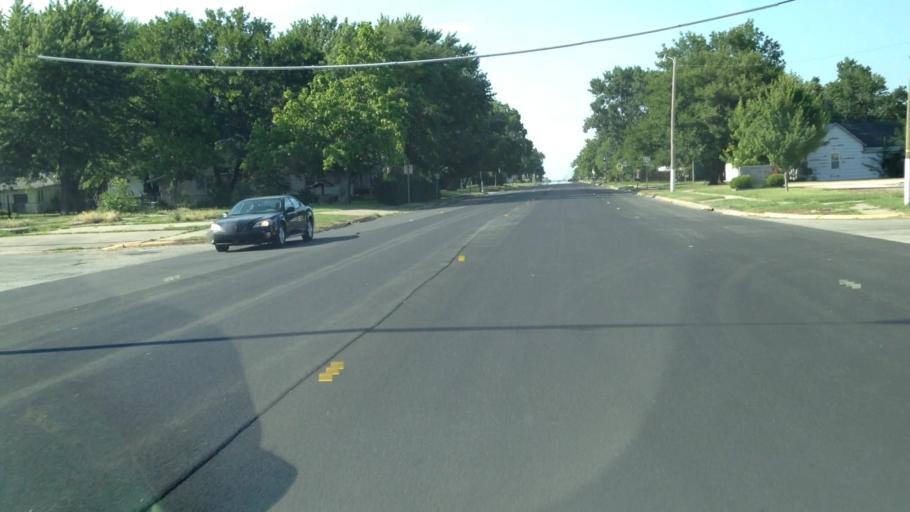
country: US
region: Kansas
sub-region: Allen County
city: Iola
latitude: 37.9165
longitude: -95.1701
